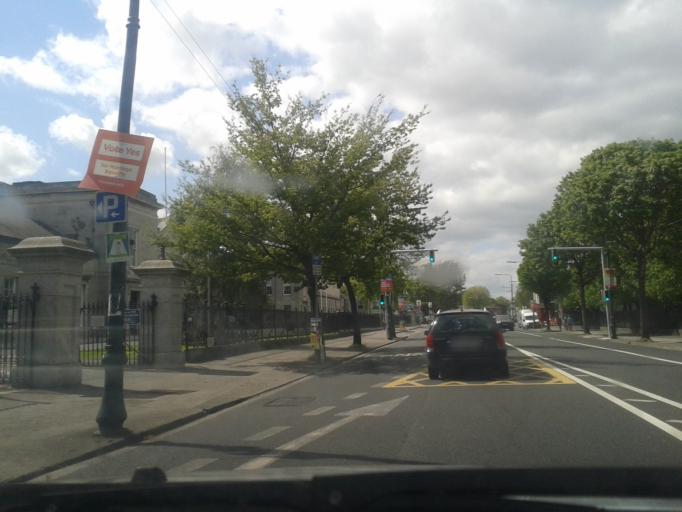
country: IE
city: Clonskeagh
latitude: 53.3280
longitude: -6.2275
